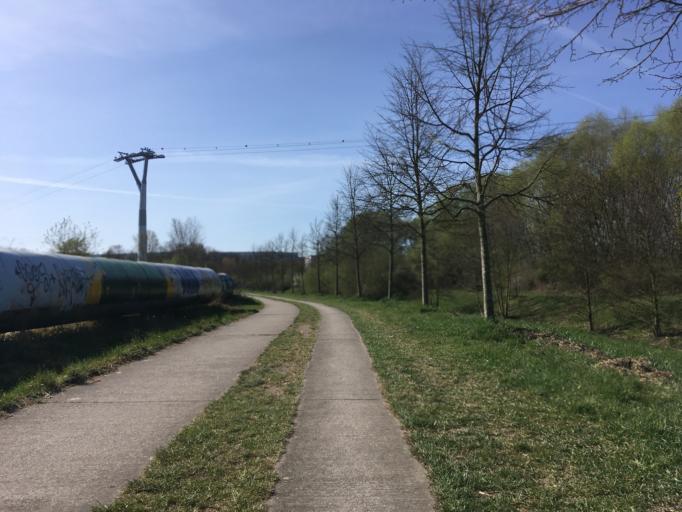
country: DE
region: Berlin
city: Kaulsdorf
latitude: 52.5329
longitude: 13.5876
